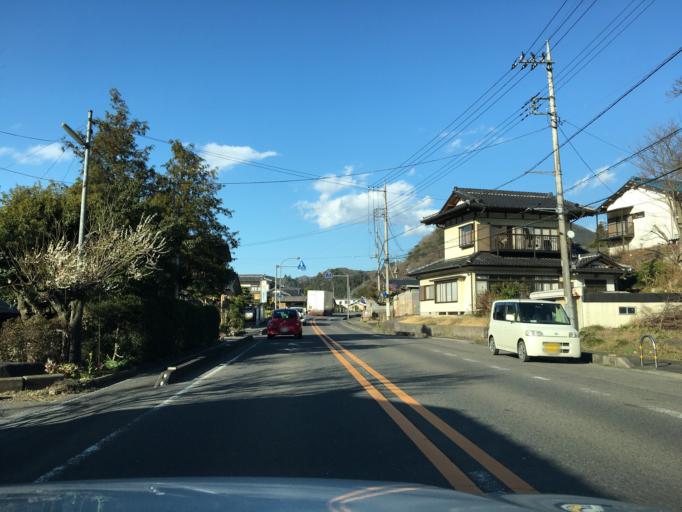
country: JP
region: Ibaraki
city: Daigo
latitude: 36.7084
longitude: 140.3839
